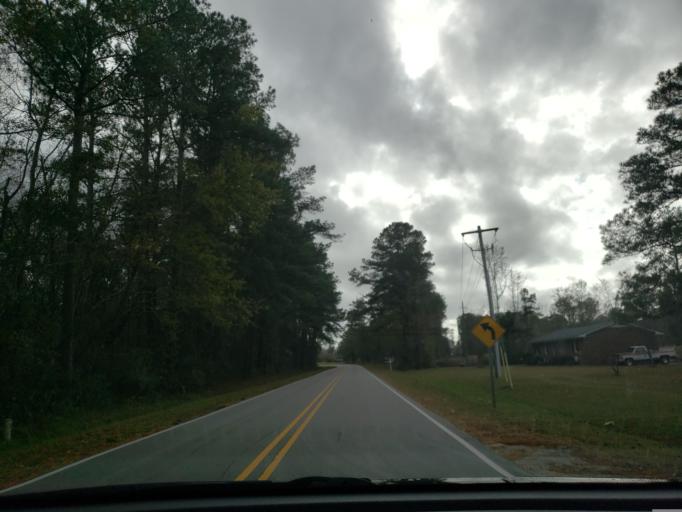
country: US
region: North Carolina
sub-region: Onslow County
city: Jacksonville
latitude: 34.7123
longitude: -77.5791
